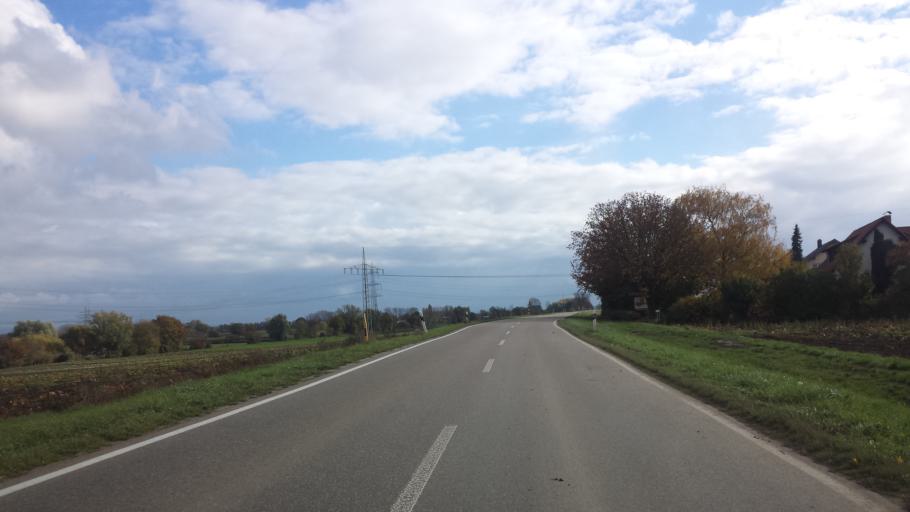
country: DE
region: Rheinland-Pfalz
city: Dannstadt-Schauernheim
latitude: 49.4167
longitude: 8.3285
